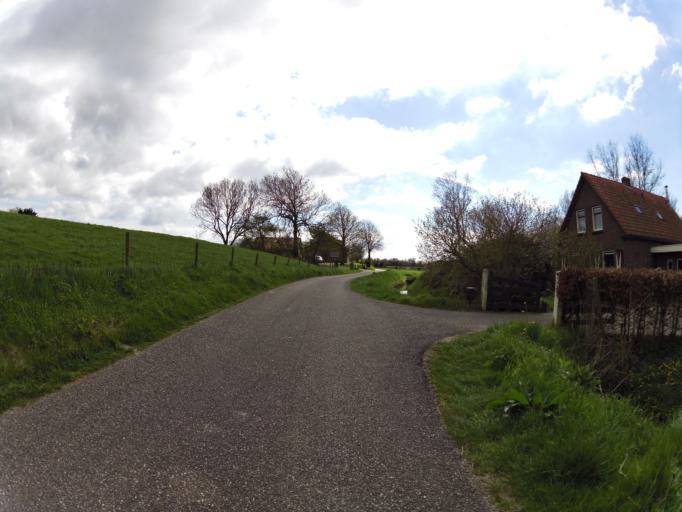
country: NL
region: South Holland
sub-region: Gemeente Hellevoetsluis
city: Nieuw-Helvoet
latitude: 51.8898
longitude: 4.0794
